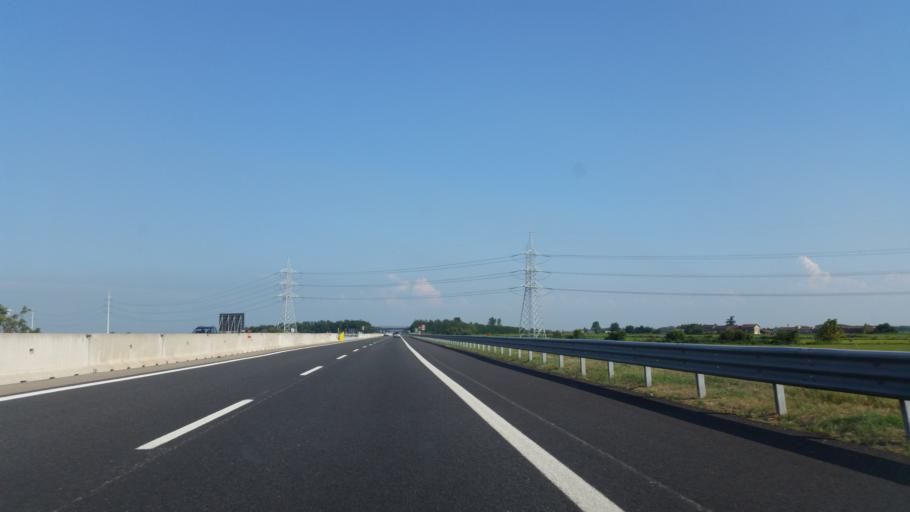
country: IT
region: Piedmont
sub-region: Provincia di Vercelli
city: Asigliano Vercellese
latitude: 45.2877
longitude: 8.3946
